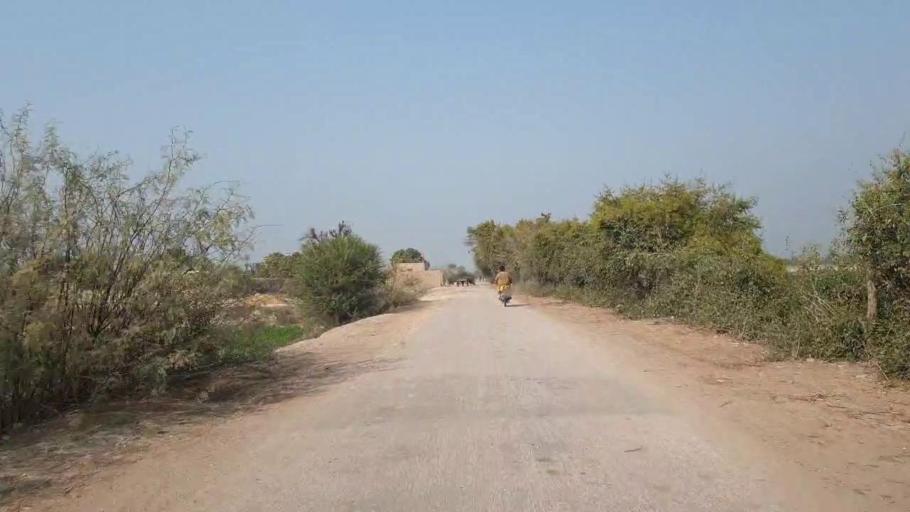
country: PK
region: Sindh
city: Hala
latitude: 25.8553
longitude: 68.4619
